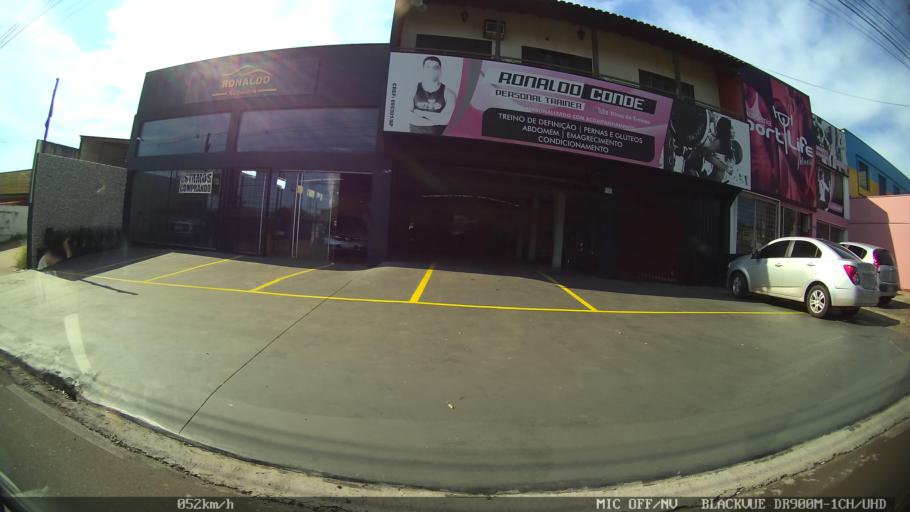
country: BR
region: Sao Paulo
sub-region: Araraquara
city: Araraquara
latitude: -21.8024
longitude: -48.1668
